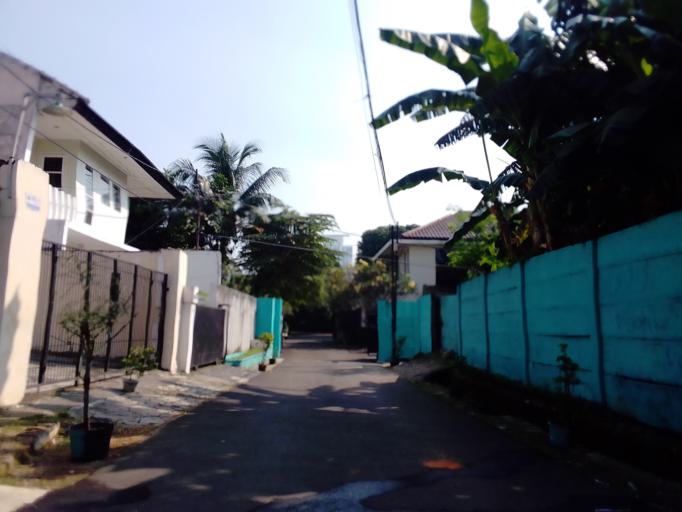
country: ID
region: Jakarta Raya
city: Jakarta
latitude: -6.2648
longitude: 106.8051
